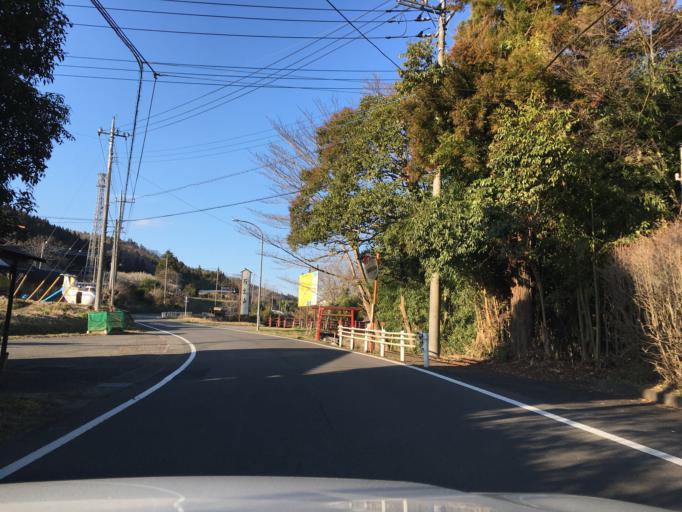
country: JP
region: Tochigi
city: Karasuyama
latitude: 36.7669
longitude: 140.2052
